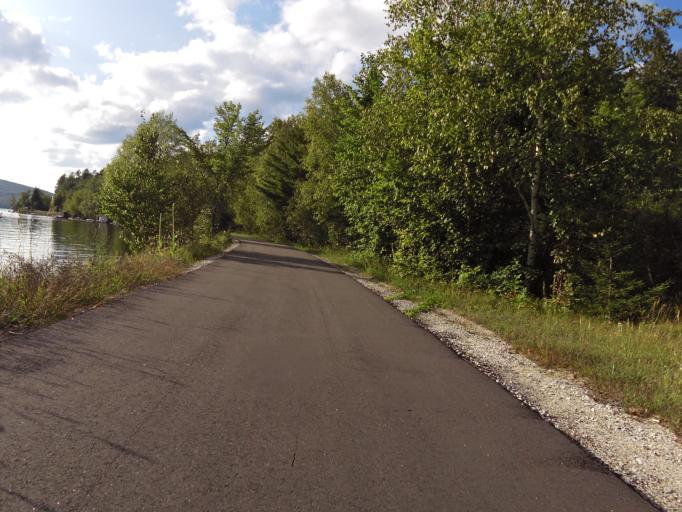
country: CA
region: Quebec
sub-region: Outaouais
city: Maniwaki
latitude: 46.2124
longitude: -76.0392
